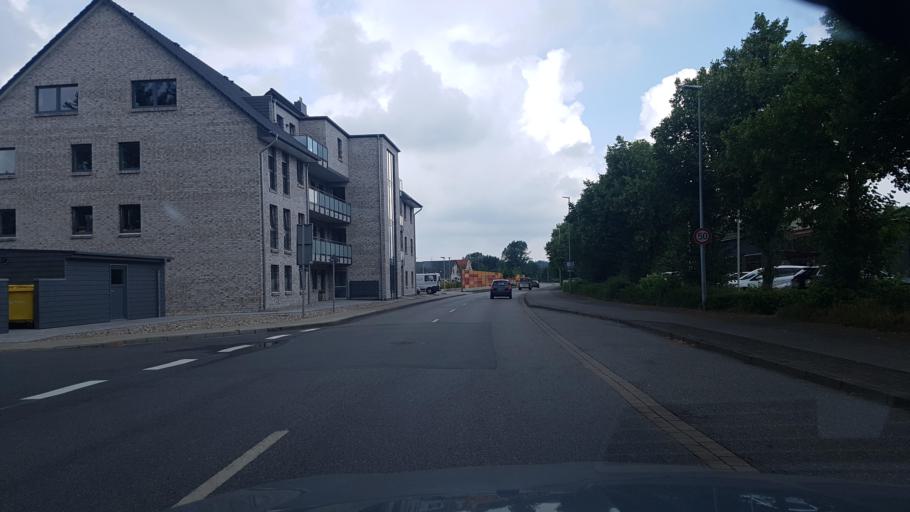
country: DE
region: Schleswig-Holstein
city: Husum
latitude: 54.4919
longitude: 9.0346
